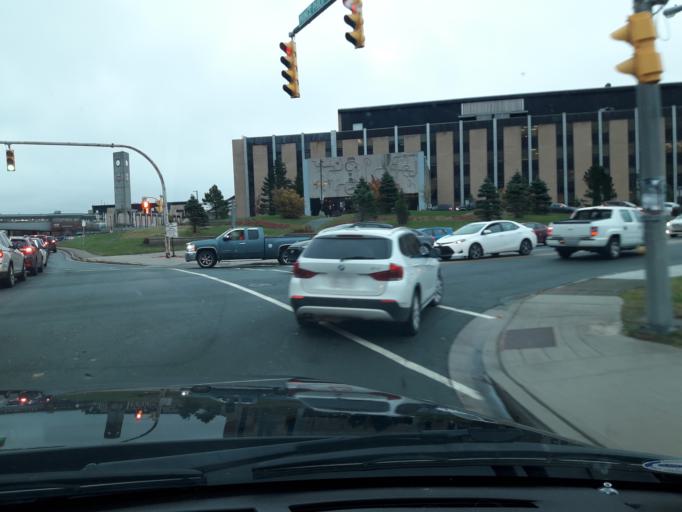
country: CA
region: Newfoundland and Labrador
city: St. John's
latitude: 47.5711
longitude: -52.7375
